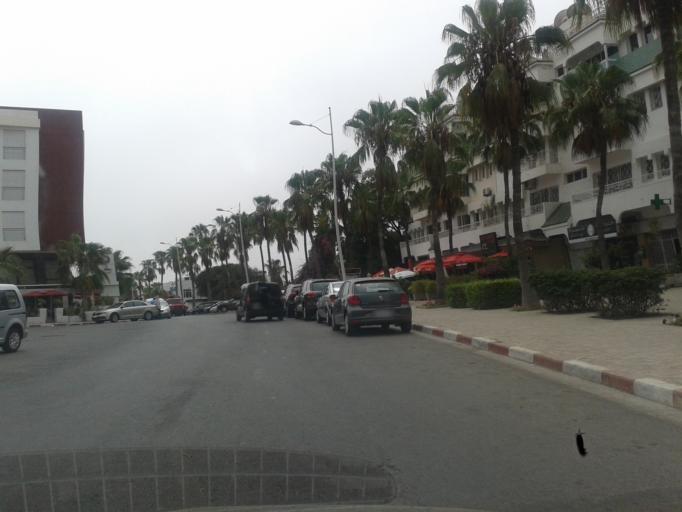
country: MA
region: Souss-Massa-Draa
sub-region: Agadir-Ida-ou-Tnan
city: Agadir
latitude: 30.4238
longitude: -9.6054
